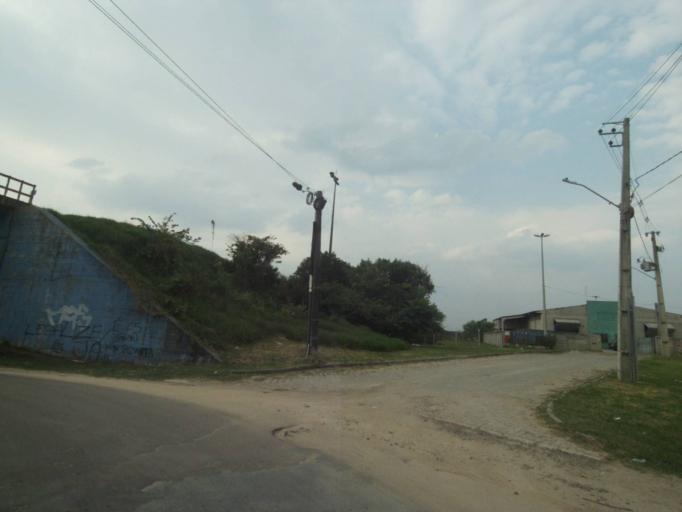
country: BR
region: Parana
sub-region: Sao Jose Dos Pinhais
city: Sao Jose dos Pinhais
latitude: -25.5296
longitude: -49.2293
